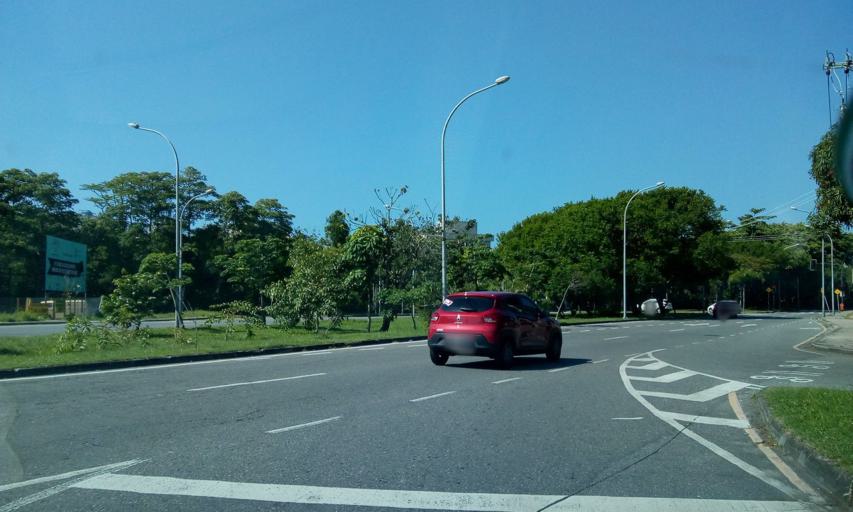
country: BR
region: Rio de Janeiro
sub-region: Nilopolis
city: Nilopolis
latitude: -23.0204
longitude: -43.4538
